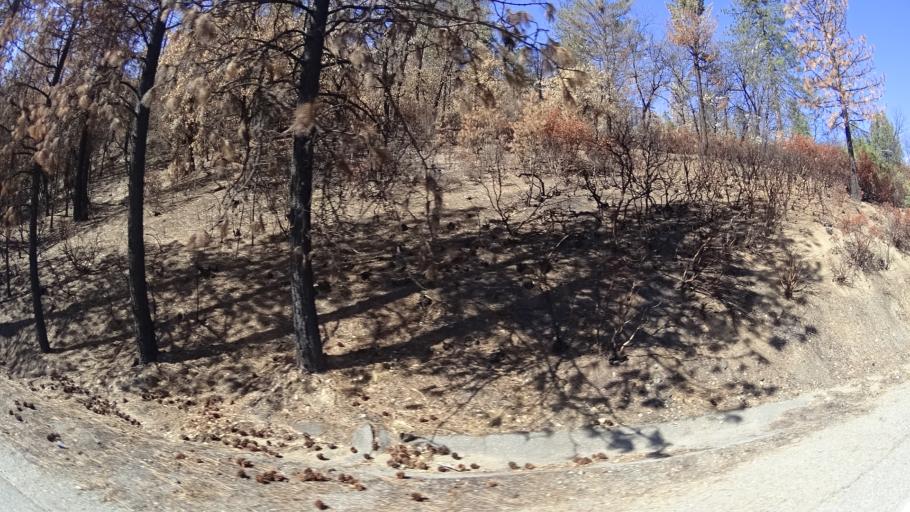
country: US
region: California
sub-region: Tehama County
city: Rancho Tehama Reserve
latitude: 39.6750
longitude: -122.6986
